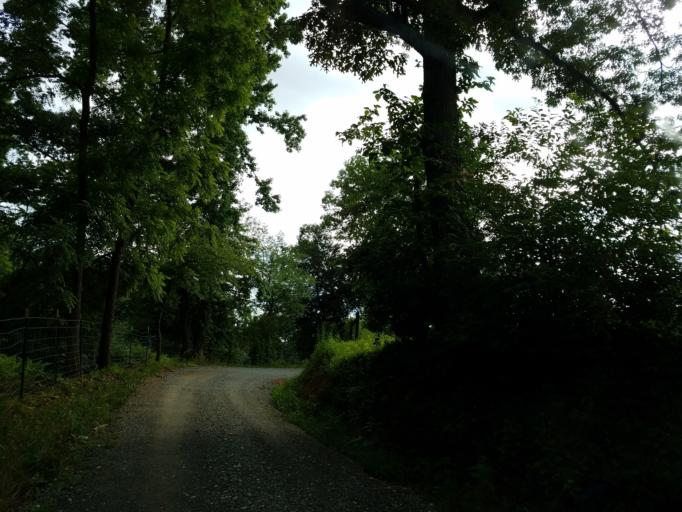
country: US
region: Georgia
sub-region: Pickens County
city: Jasper
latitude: 34.5429
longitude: -84.5328
